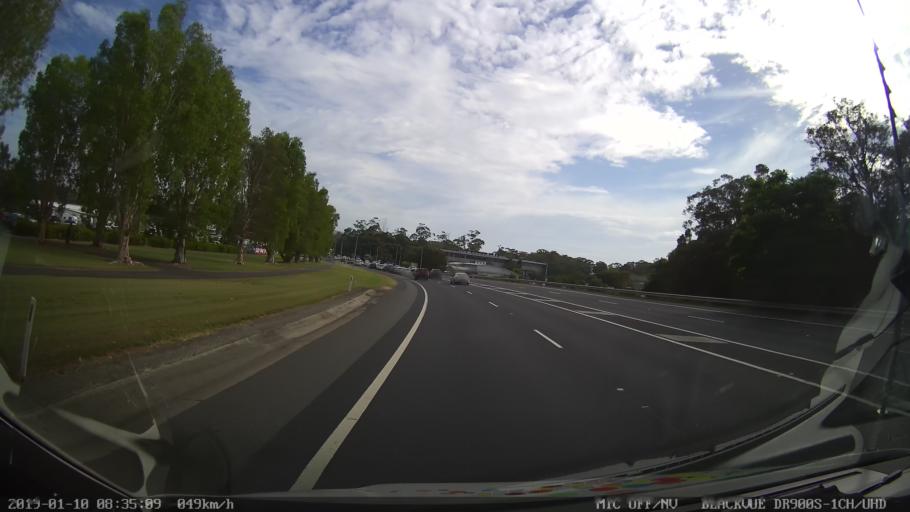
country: AU
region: New South Wales
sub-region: Coffs Harbour
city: Boambee
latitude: -30.3182
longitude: 153.0906
